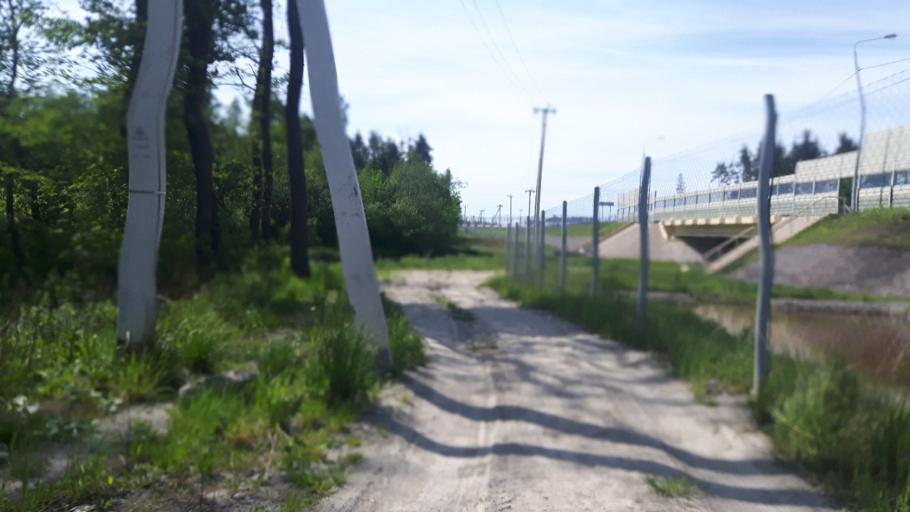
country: RU
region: Leningrad
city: Vistino
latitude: 59.6750
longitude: 28.4366
